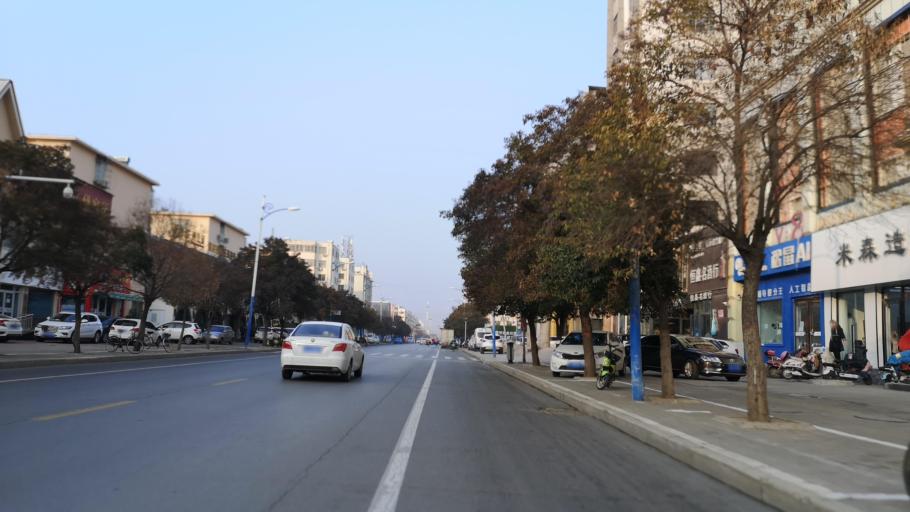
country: CN
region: Henan Sheng
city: Zhongyuanlu
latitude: 35.7674
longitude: 115.0633
